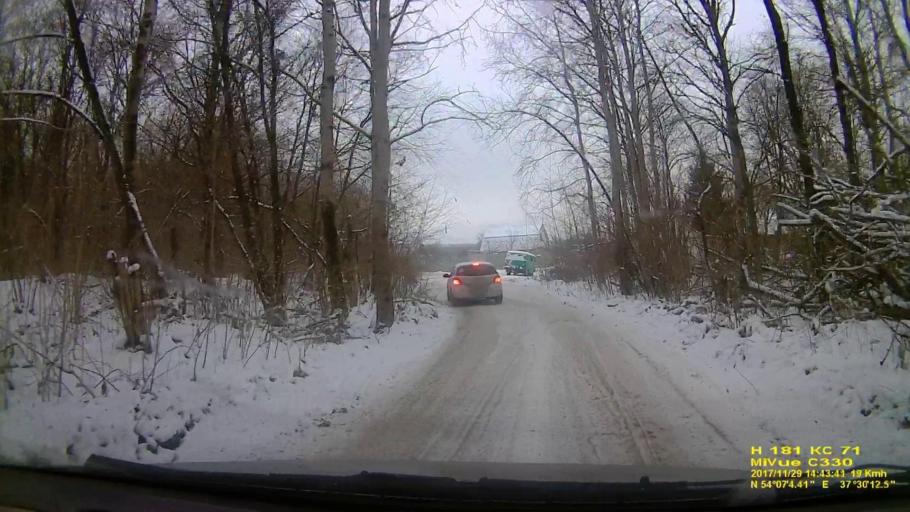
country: RU
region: Tula
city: Kosaya Gora
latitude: 54.1179
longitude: 37.5035
